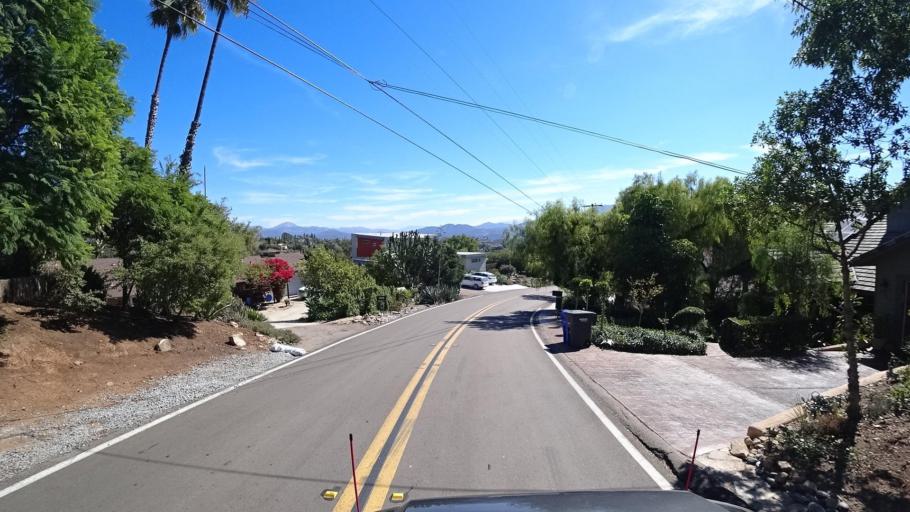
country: US
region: California
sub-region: San Diego County
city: Casa de Oro-Mount Helix
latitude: 32.7605
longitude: -116.9649
